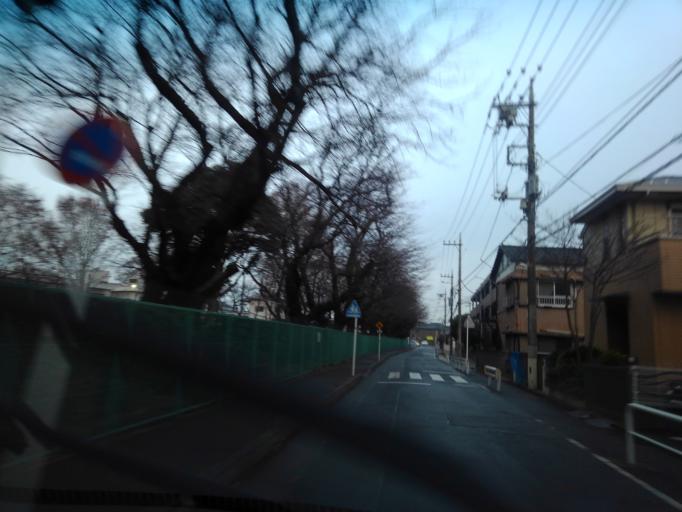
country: JP
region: Tokyo
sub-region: Machida-shi
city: Machida
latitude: 35.5195
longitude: 139.4416
